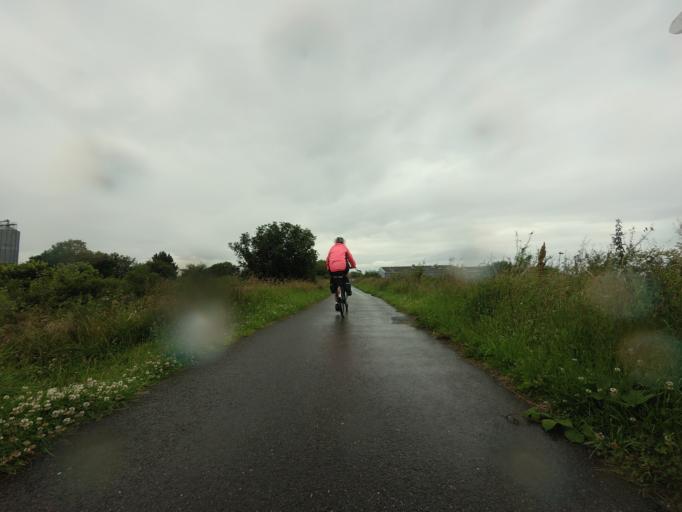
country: GB
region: Scotland
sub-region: Moray
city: Buckie
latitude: 57.6807
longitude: -2.9439
